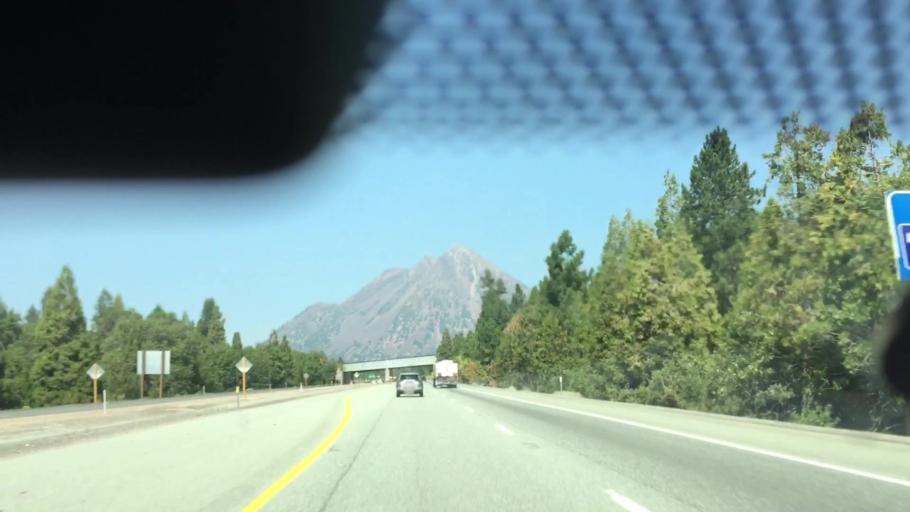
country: US
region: California
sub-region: Siskiyou County
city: Mount Shasta
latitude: 41.3260
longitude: -122.3301
